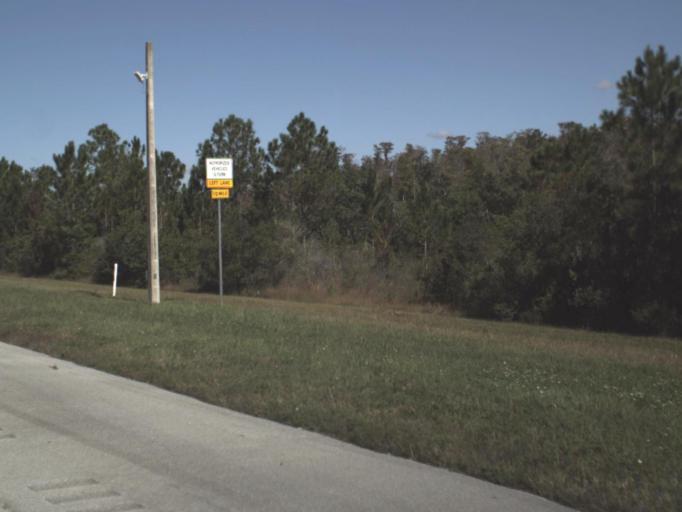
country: US
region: Florida
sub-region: Osceola County
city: Saint Cloud
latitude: 27.9608
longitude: -81.0992
